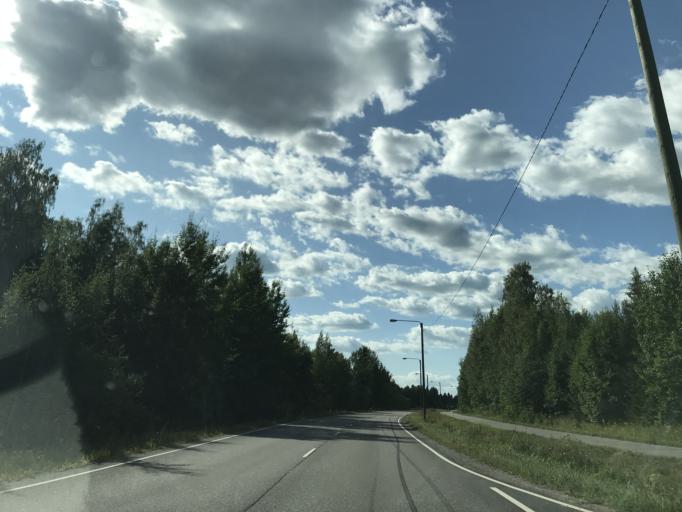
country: FI
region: Uusimaa
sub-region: Helsinki
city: Nurmijaervi
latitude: 60.4356
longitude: 24.8378
